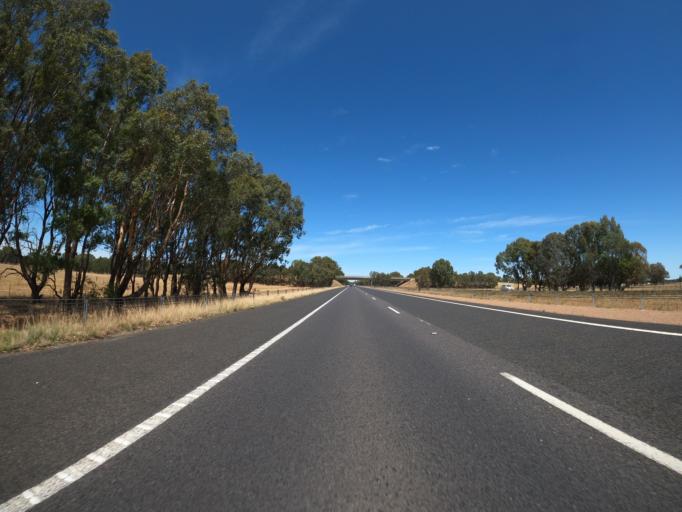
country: AU
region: Victoria
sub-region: Benalla
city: Benalla
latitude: -36.5603
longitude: 146.0192
